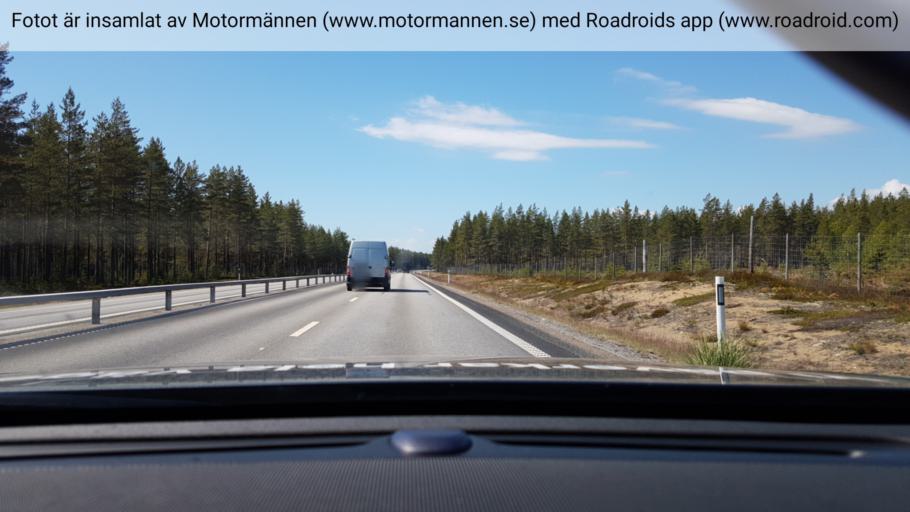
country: SE
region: Vaesterbotten
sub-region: Umea Kommun
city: Hoernefors
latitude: 63.5939
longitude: 19.7080
